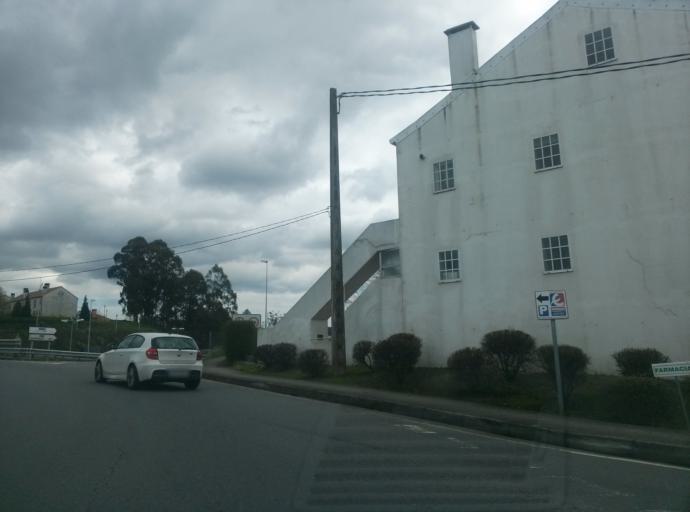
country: ES
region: Galicia
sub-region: Provincia da Coruna
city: Santiago de Compostela
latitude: 42.8635
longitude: -8.5675
